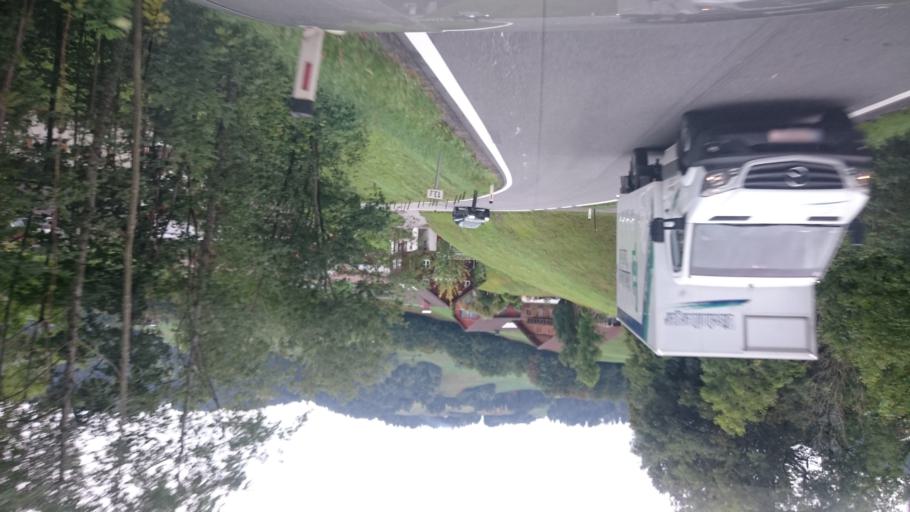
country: AT
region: Vorarlberg
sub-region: Politischer Bezirk Bregenz
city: Andelsbuch
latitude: 47.4165
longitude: 9.8492
